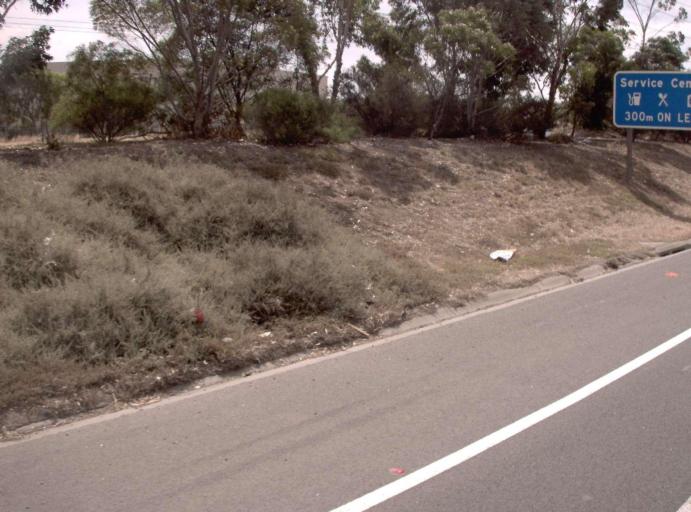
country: AU
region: Victoria
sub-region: Brimbank
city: Sunshine West
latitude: -37.8097
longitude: 144.8077
